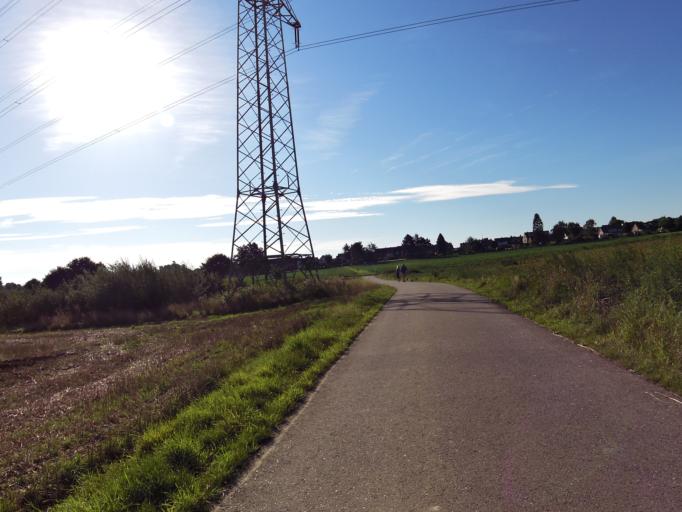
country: DE
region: North Rhine-Westphalia
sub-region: Regierungsbezirk Koln
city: Alsdorf
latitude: 50.8873
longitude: 6.1637
